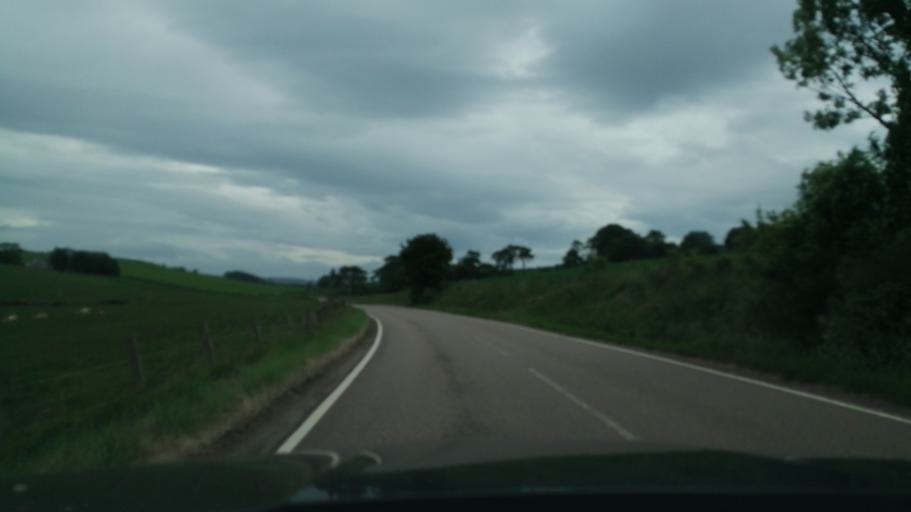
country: GB
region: Scotland
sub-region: Moray
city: Cullen
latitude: 57.6154
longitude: -2.8484
